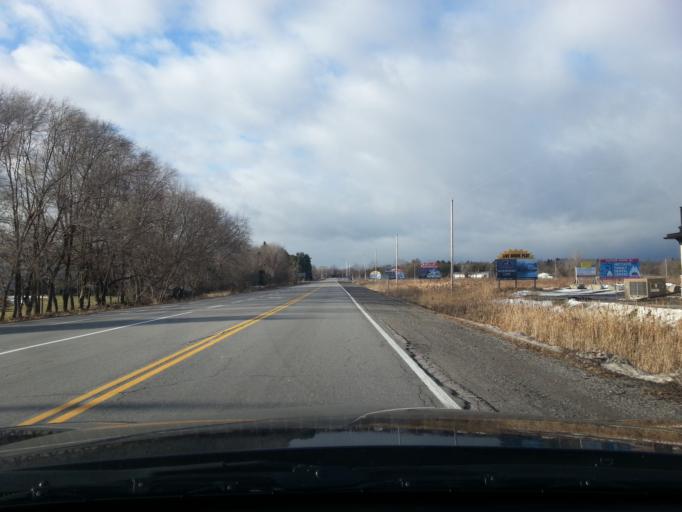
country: CA
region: Ontario
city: Ottawa
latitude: 45.2618
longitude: -75.5522
